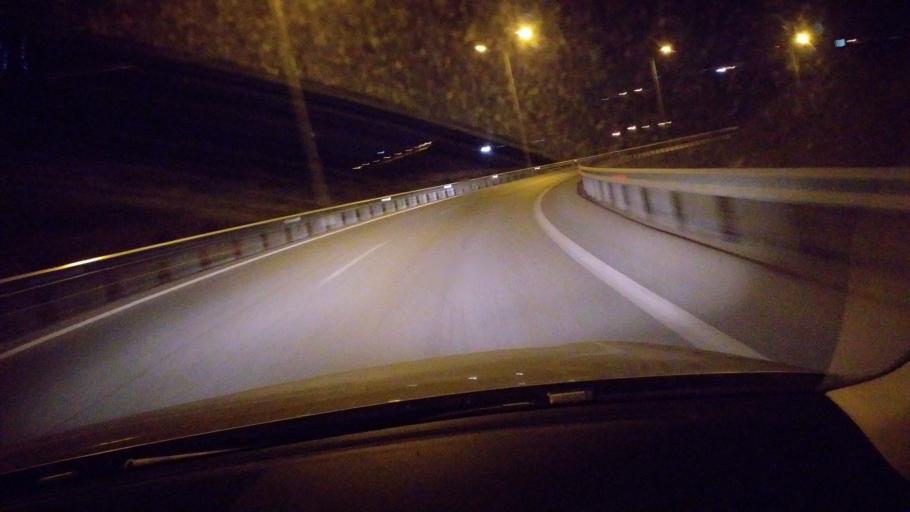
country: TR
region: Ankara
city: Ankara
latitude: 40.0240
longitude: 32.8255
